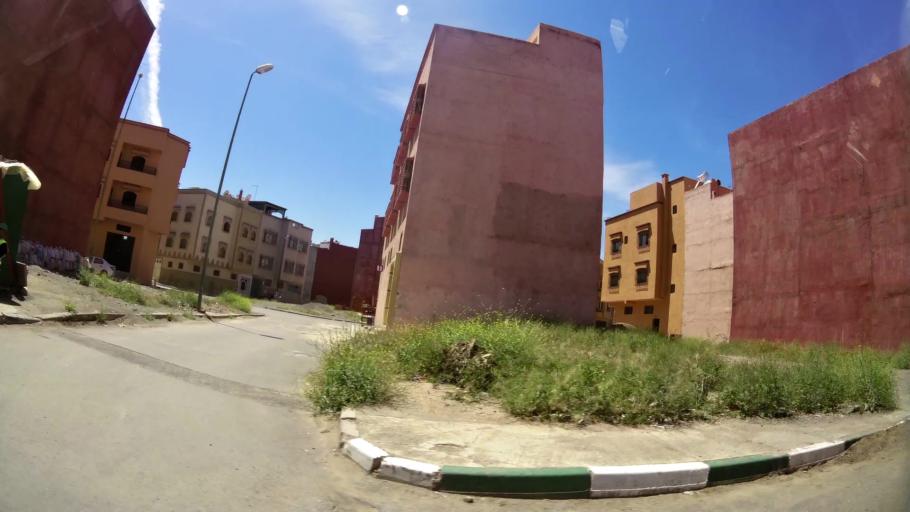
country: MA
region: Marrakech-Tensift-Al Haouz
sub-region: Marrakech
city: Marrakesh
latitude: 31.6395
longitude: -8.0481
